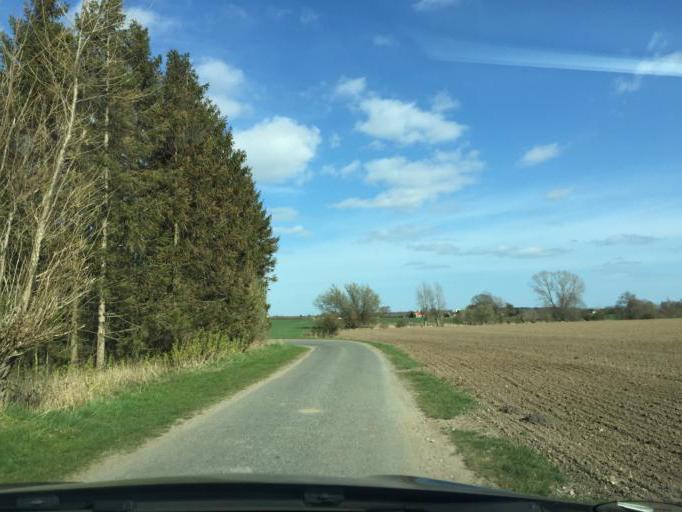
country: DK
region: South Denmark
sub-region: Faaborg-Midtfyn Kommune
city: Arslev
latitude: 55.3060
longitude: 10.5188
